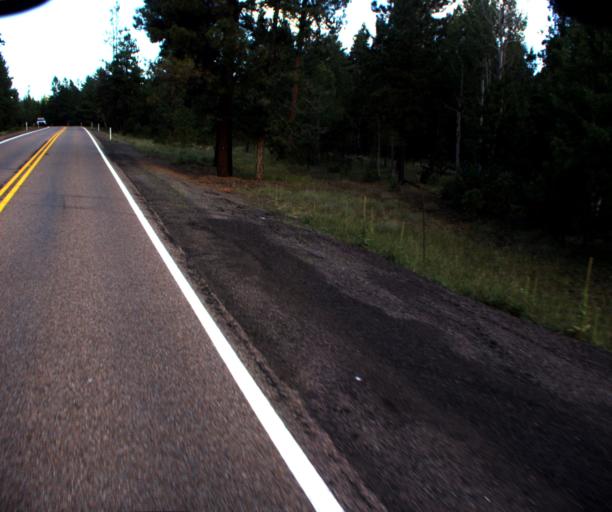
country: US
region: Arizona
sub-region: Navajo County
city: Pinetop-Lakeside
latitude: 34.0247
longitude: -109.6500
